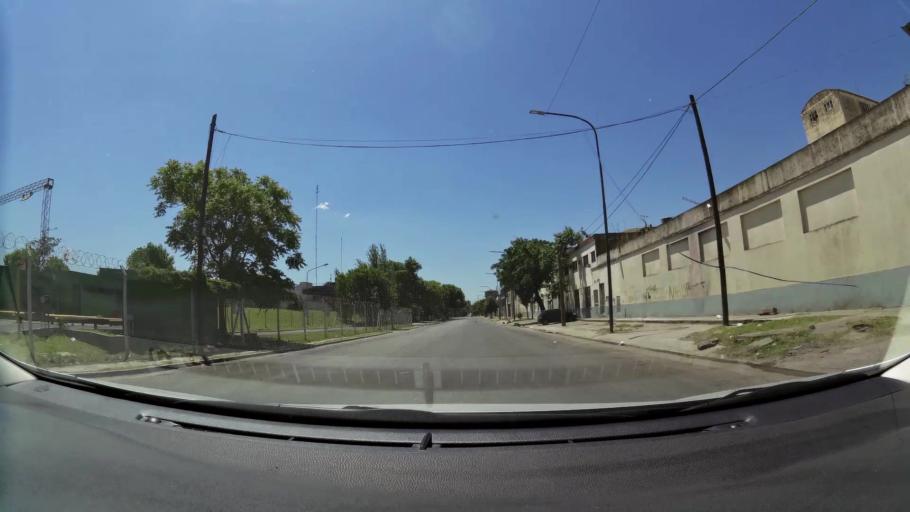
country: AR
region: Buenos Aires
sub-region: Partido de Avellaneda
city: Avellaneda
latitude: -34.6487
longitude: -58.4011
